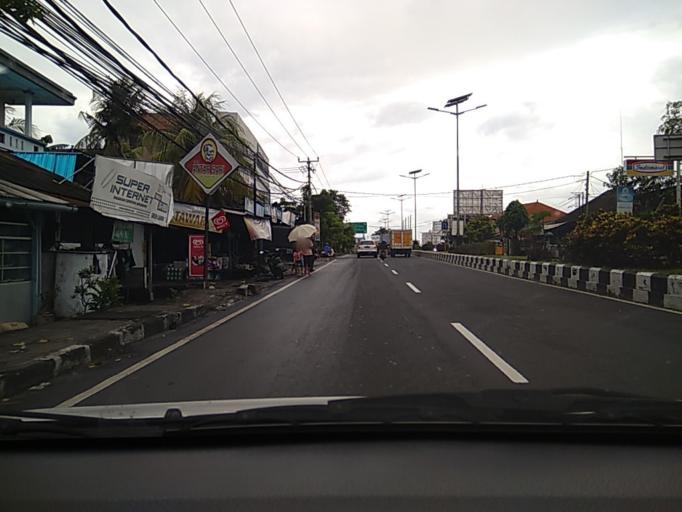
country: ID
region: Bali
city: Bualu
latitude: -8.7920
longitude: 115.2141
